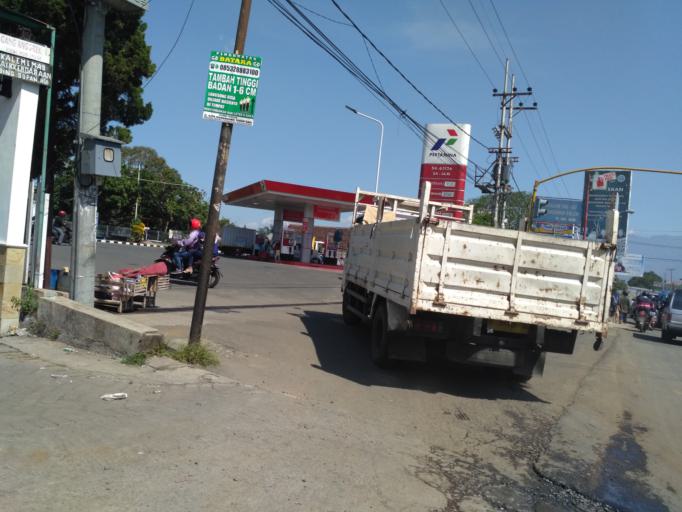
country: ID
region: East Java
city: Tamiajeng
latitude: -7.9527
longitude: 112.6903
